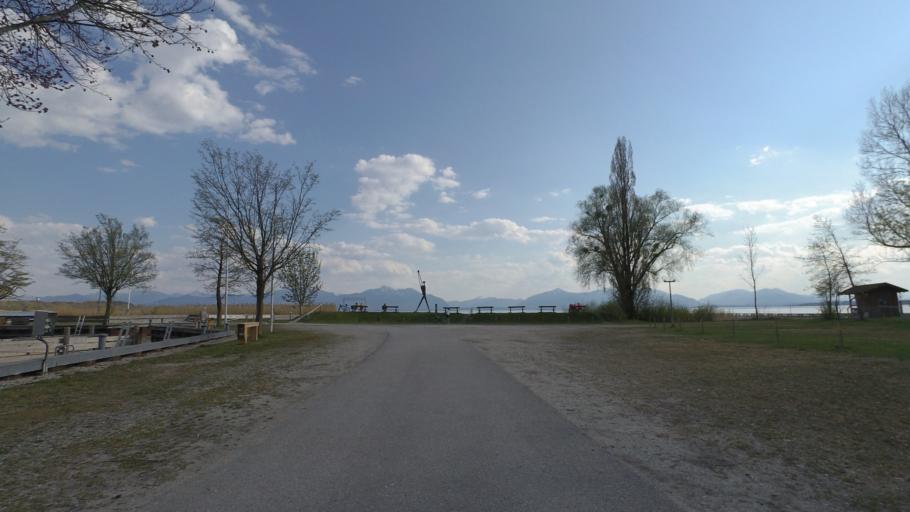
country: DE
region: Bavaria
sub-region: Upper Bavaria
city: Seeon-Seebruck
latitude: 47.9306
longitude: 12.4798
